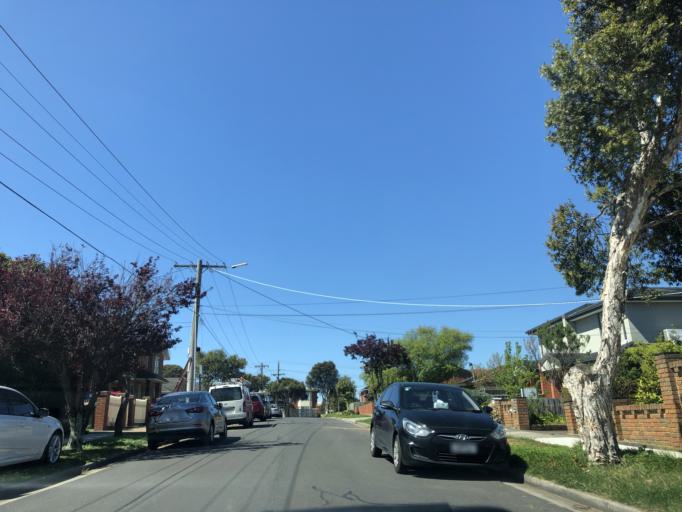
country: AU
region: Victoria
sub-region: Monash
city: Clayton
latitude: -37.9179
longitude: 145.1288
